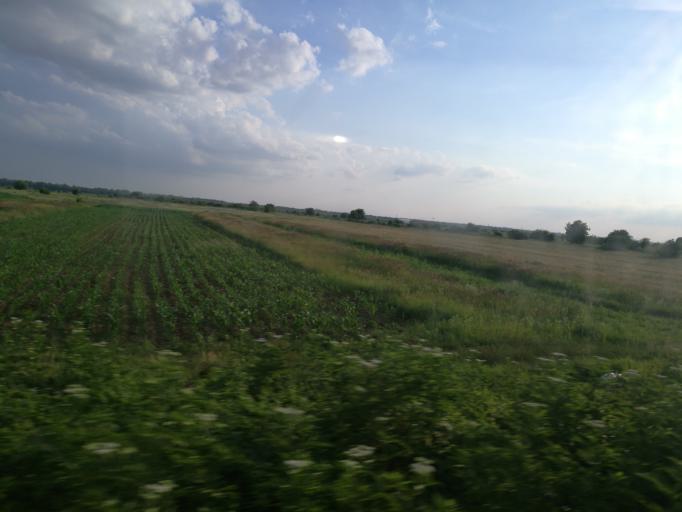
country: RO
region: Arges
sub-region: Oras Topoloveni
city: Topoloveni
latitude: 44.7982
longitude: 25.0969
